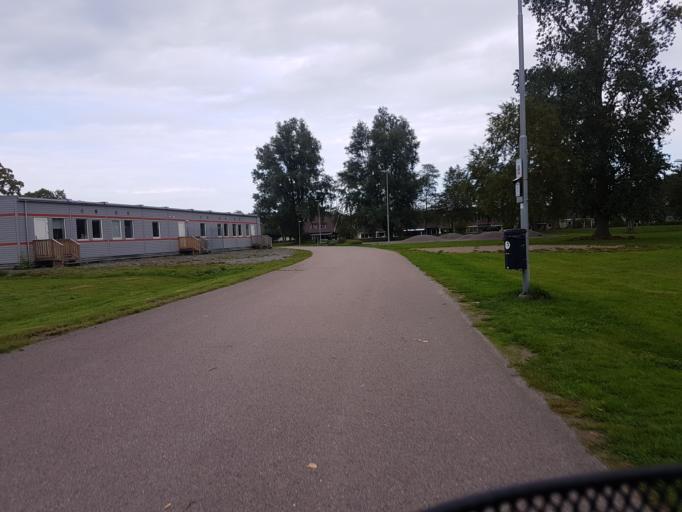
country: SE
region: Vaestra Goetaland
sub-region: Ale Kommun
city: Nodinge-Nol
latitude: 57.8939
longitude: 12.0534
